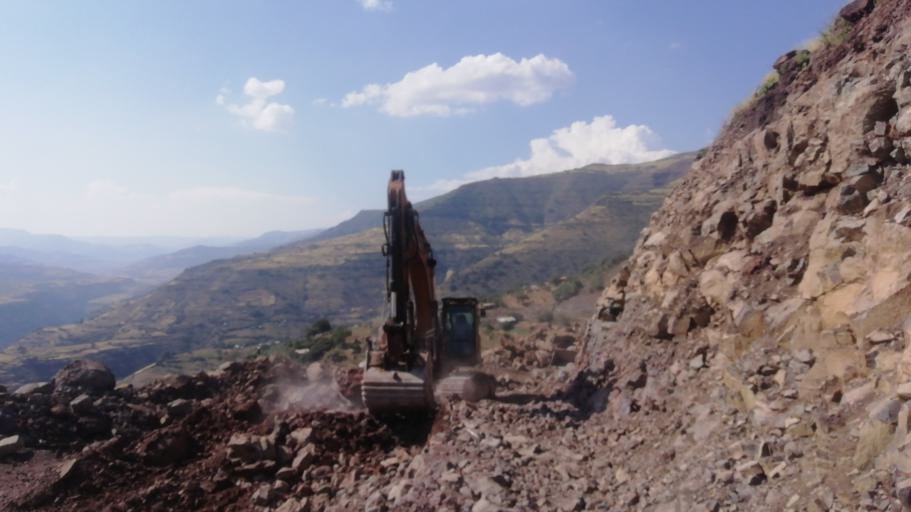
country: ET
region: Amhara
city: Addiet Canna
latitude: 11.2299
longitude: 37.8872
